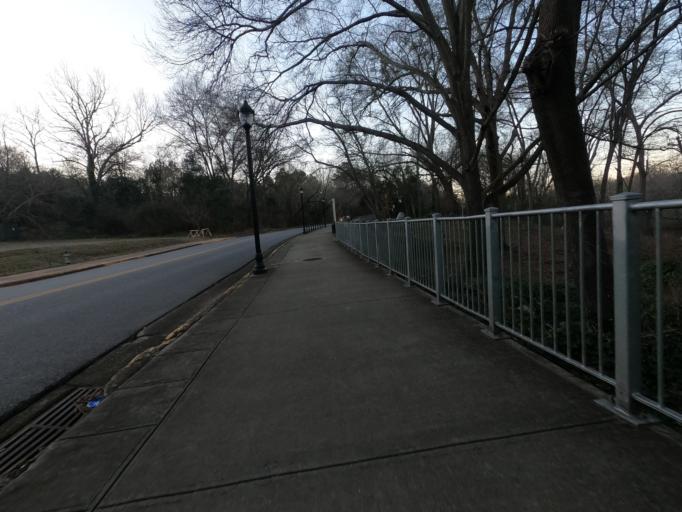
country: US
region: Georgia
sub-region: Clarke County
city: Athens
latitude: 33.9604
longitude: -83.3690
